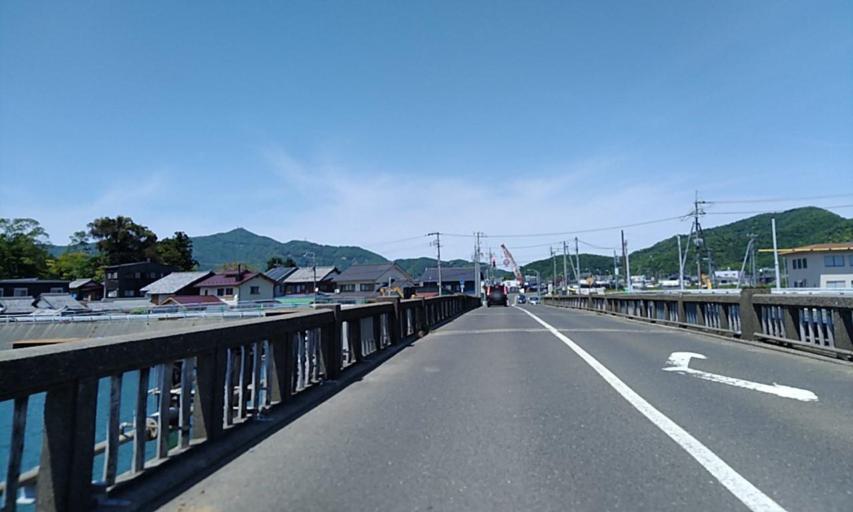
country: JP
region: Fukui
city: Obama
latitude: 35.5023
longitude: 135.7469
